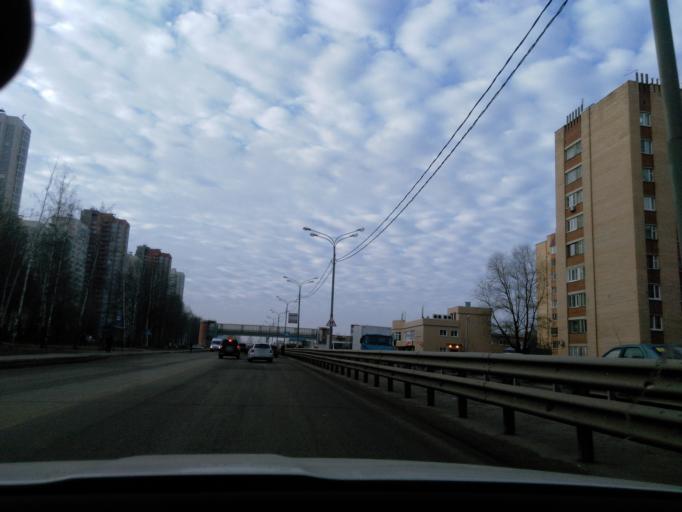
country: RU
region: Moskovskaya
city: Dolgoprudnyy
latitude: 55.9370
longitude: 37.4920
